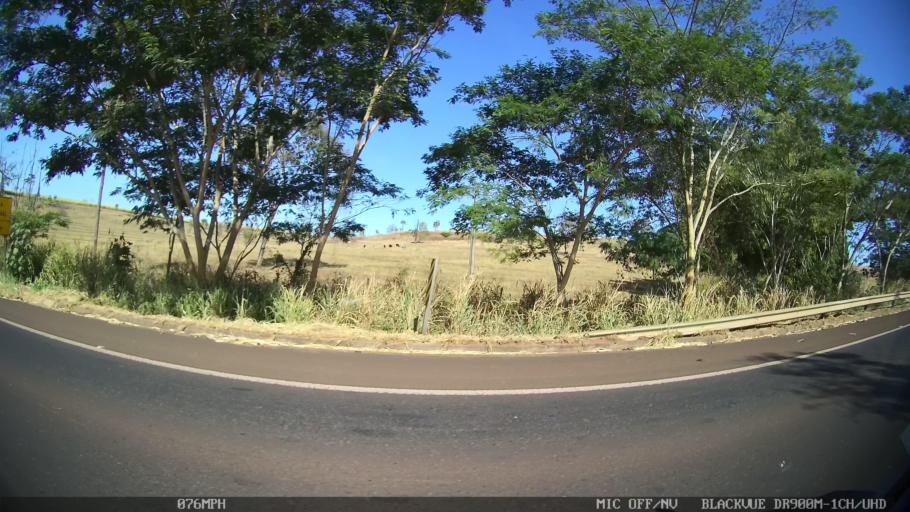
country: BR
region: Sao Paulo
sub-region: Barretos
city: Barretos
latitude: -20.6034
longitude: -48.7335
